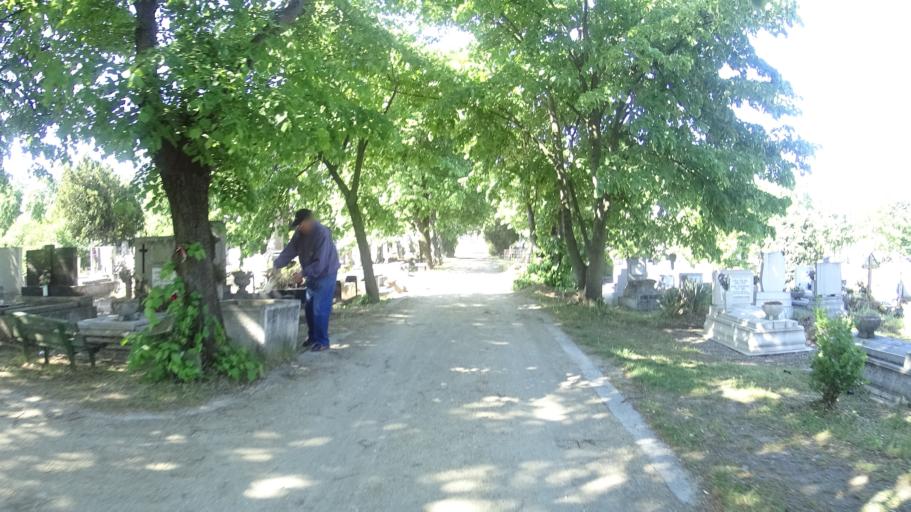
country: HU
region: Budapest
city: Budapest XXIII. keruelet
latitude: 47.4140
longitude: 19.1196
